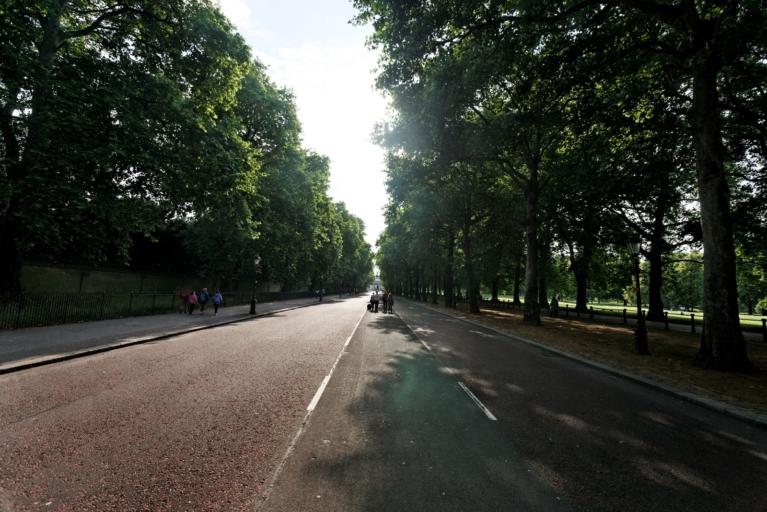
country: GB
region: England
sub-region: Greater London
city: London
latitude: 51.5022
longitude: -0.1440
